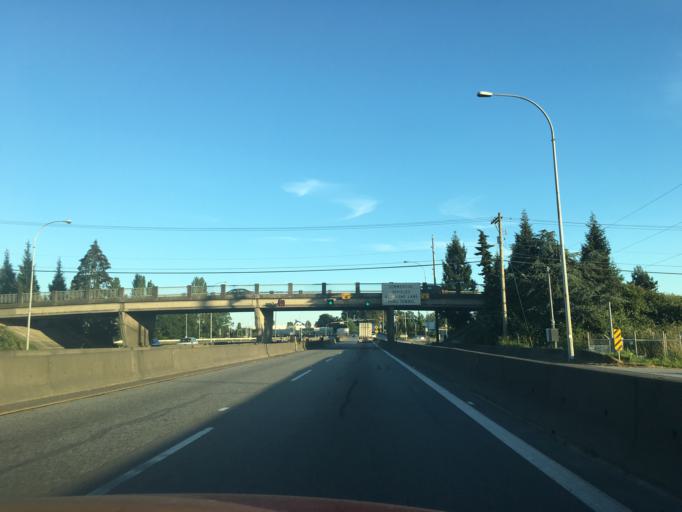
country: CA
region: British Columbia
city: Ladner
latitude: 49.1342
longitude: -123.0869
